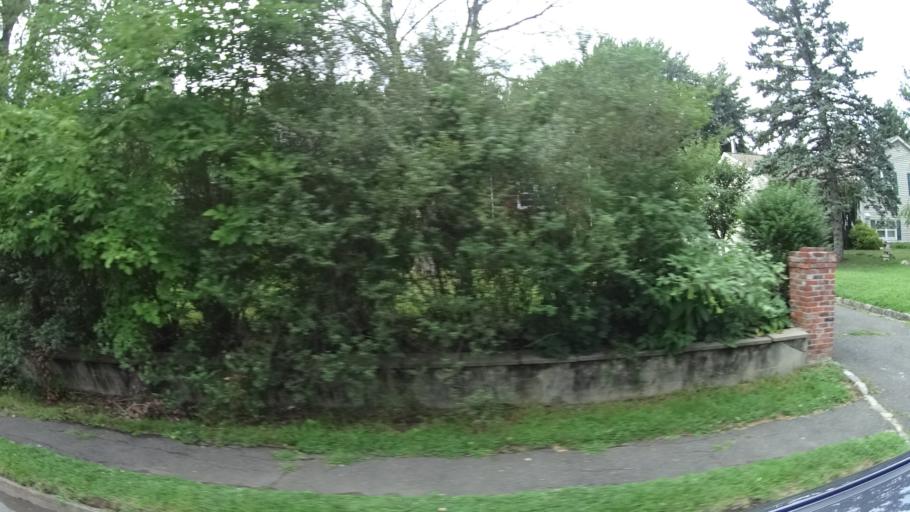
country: US
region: New Jersey
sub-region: Union County
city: Berkeley Heights
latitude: 40.6902
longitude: -74.4323
